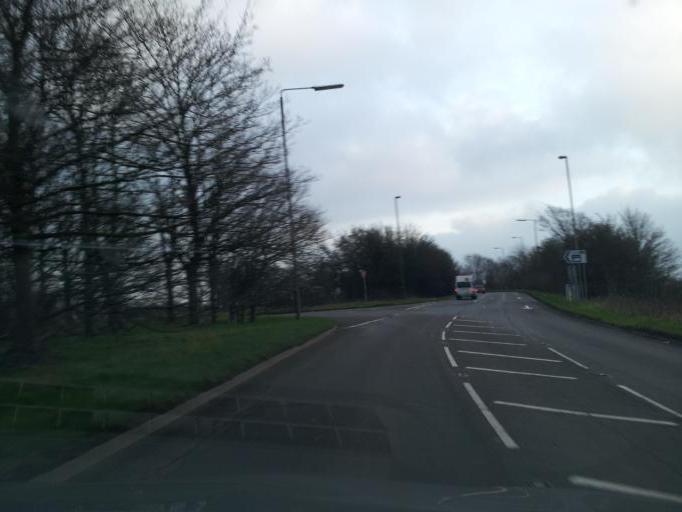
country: GB
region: England
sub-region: Derbyshire
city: Etwall
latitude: 52.8553
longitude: -1.5865
